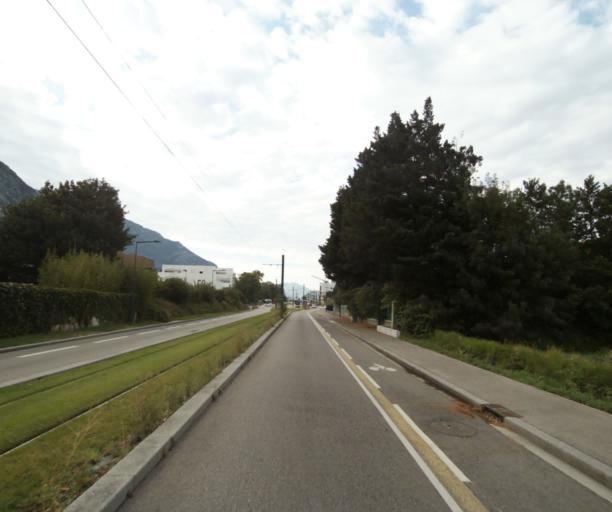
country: FR
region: Rhone-Alpes
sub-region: Departement de l'Isere
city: Fontanil-Cornillon
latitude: 45.2562
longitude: 5.6608
